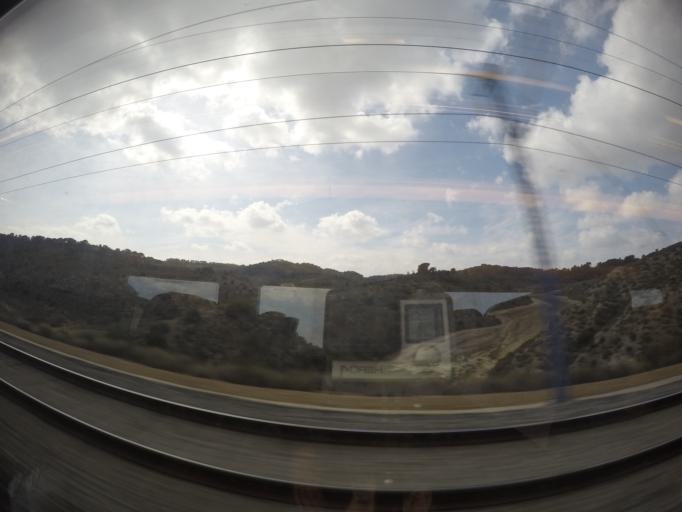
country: ES
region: Aragon
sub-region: Provincia de Zaragoza
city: Monegrillo
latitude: 41.5317
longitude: -0.3398
